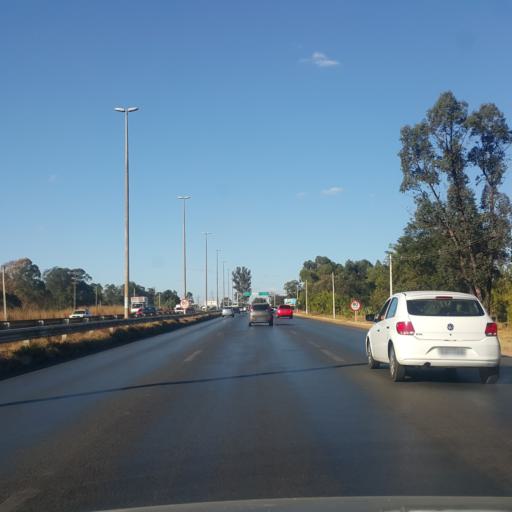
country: BR
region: Federal District
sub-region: Brasilia
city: Brasilia
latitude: -15.7943
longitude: -48.0609
